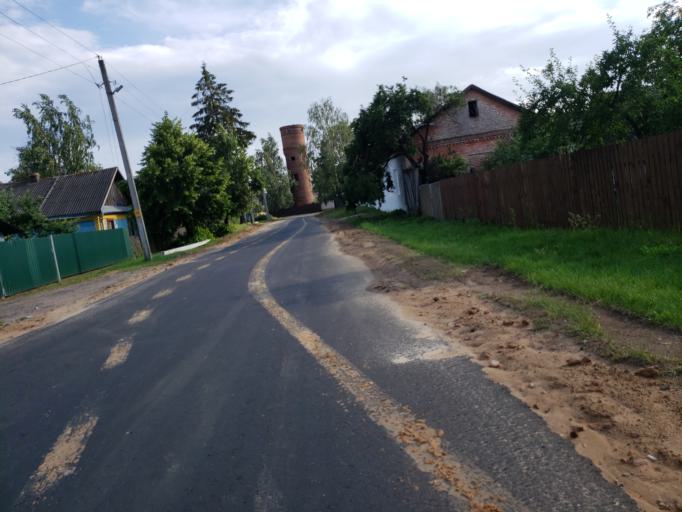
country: BY
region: Minsk
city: Chervyen'
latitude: 53.7096
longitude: 28.4169
